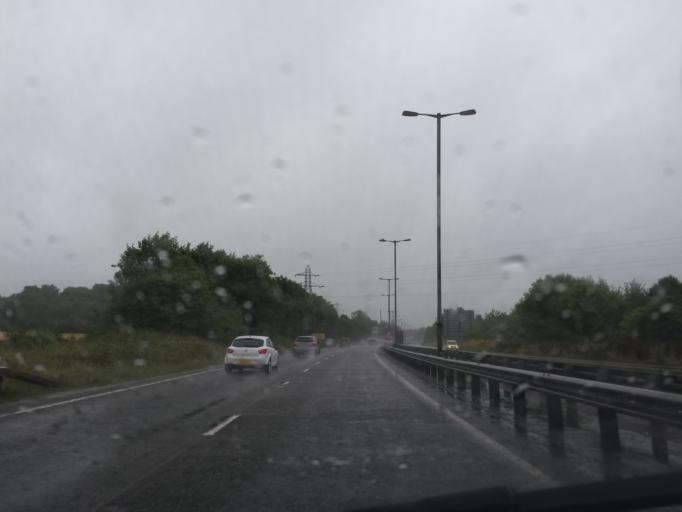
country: GB
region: England
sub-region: Warwickshire
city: Ryton on Dunsmore
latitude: 52.3945
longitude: -1.4327
